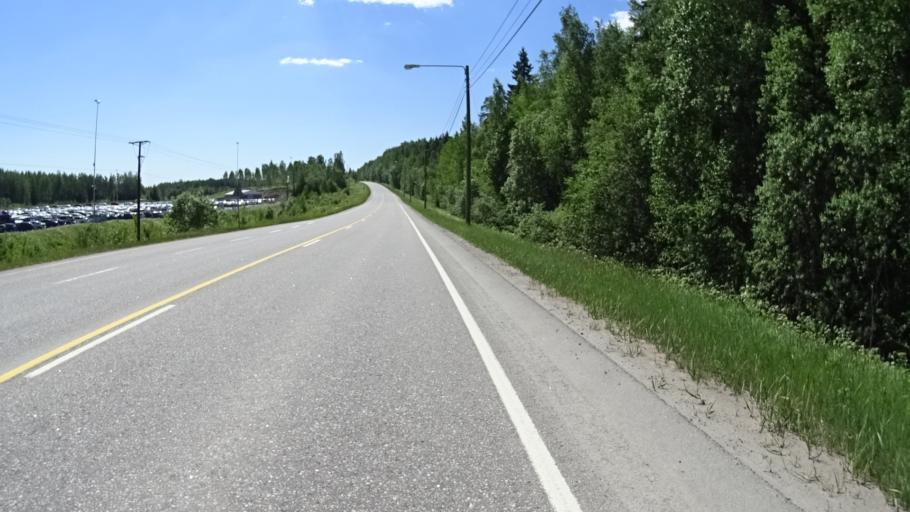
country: FI
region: Uusimaa
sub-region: Helsinki
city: Nurmijaervi
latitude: 60.3714
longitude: 24.8053
